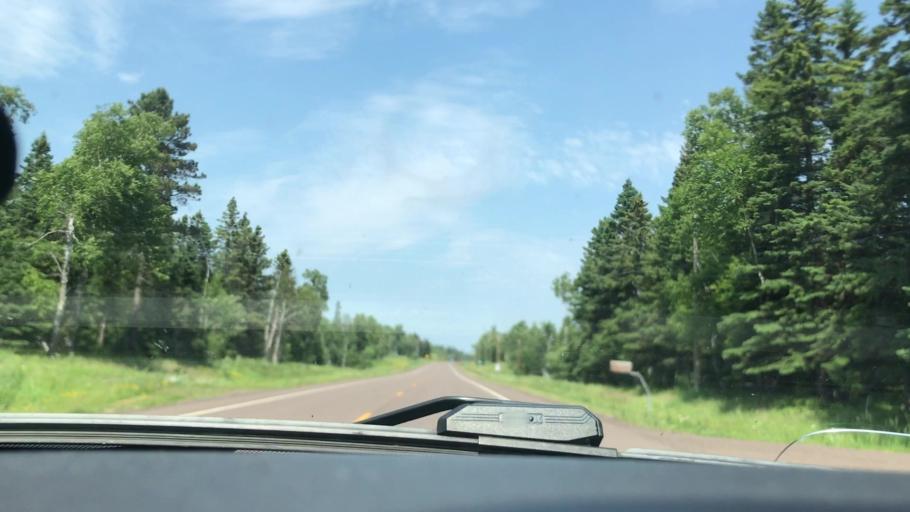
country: US
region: Minnesota
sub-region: Lake County
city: Silver Bay
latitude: 47.4258
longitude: -91.0916
